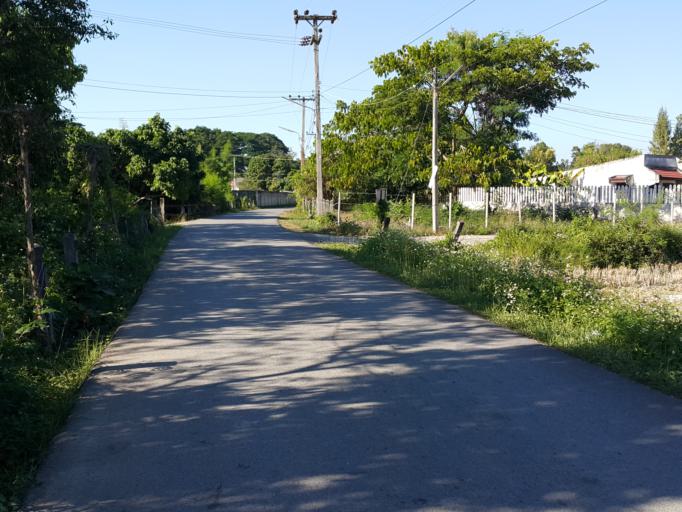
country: TH
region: Chiang Mai
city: San Kamphaeng
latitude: 18.7878
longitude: 99.1027
